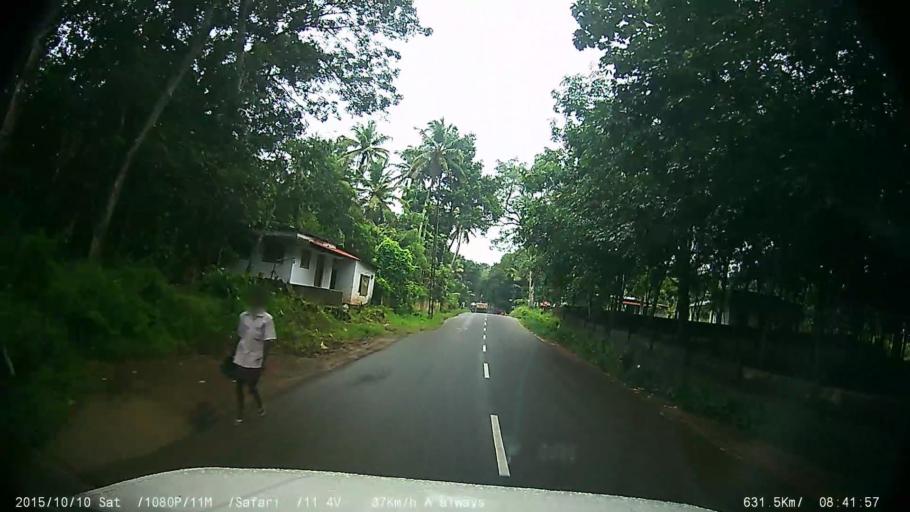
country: IN
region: Kerala
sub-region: Kottayam
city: Palackattumala
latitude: 9.7531
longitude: 76.5421
